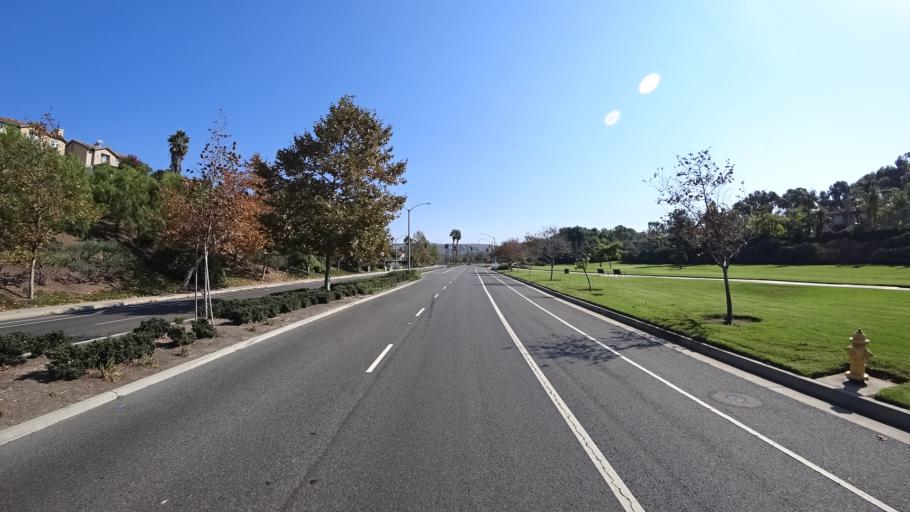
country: US
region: California
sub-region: Orange County
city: San Juan Capistrano
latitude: 33.4672
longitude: -117.6374
